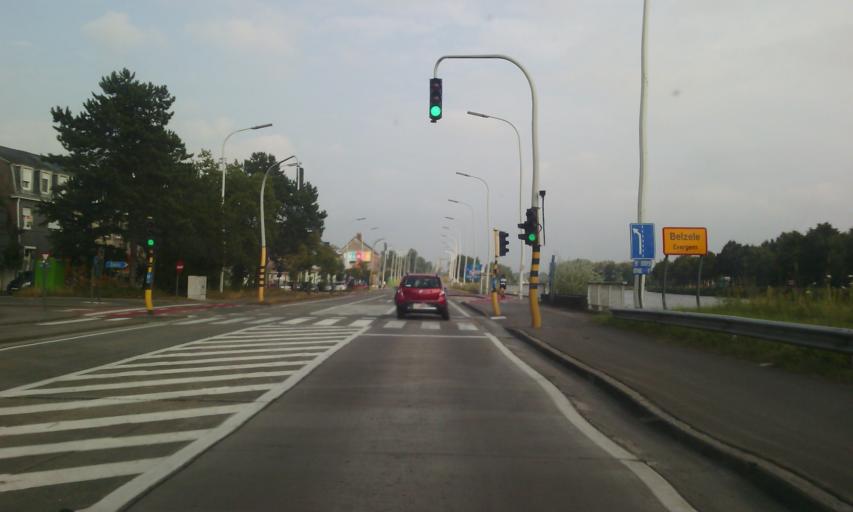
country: BE
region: Flanders
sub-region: Provincie Oost-Vlaanderen
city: Lovendegem
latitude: 51.0903
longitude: 3.6519
